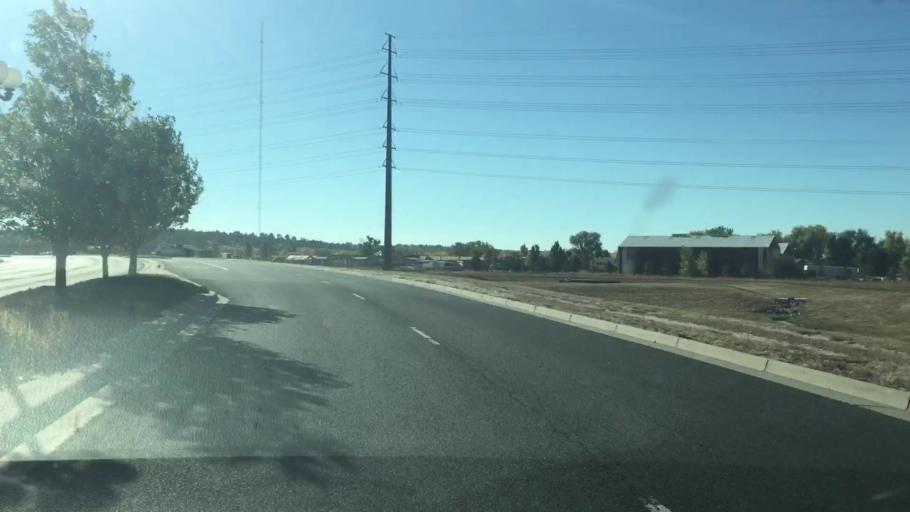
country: US
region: Colorado
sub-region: Douglas County
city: Parker
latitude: 39.5122
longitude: -104.7738
